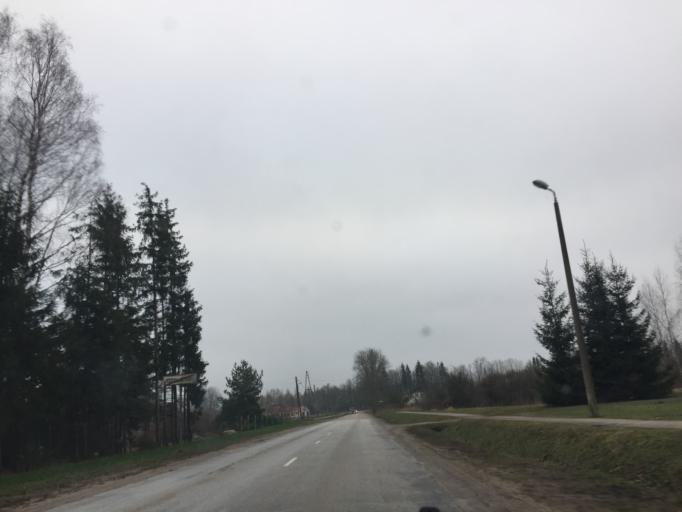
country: LV
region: Limbazu Rajons
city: Limbazi
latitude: 57.5156
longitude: 24.6895
